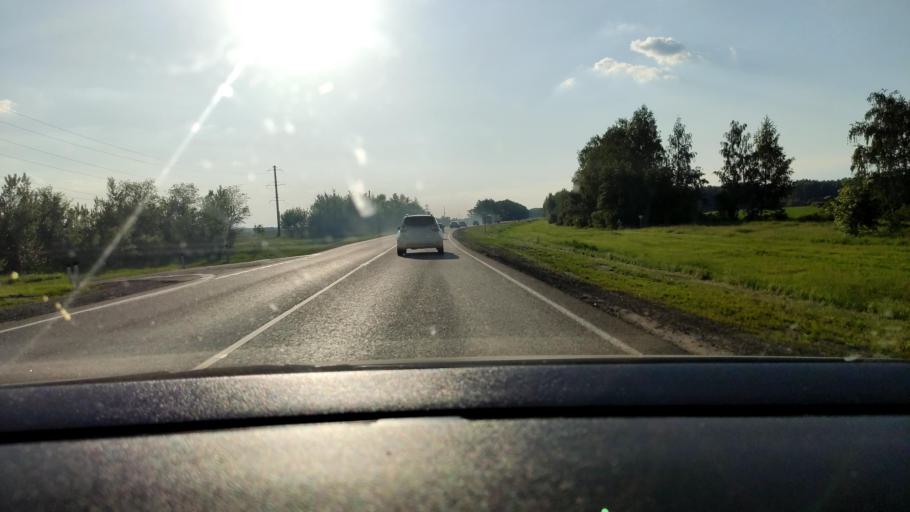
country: RU
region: Voronezj
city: Kashirskoye
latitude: 51.4787
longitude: 39.6693
